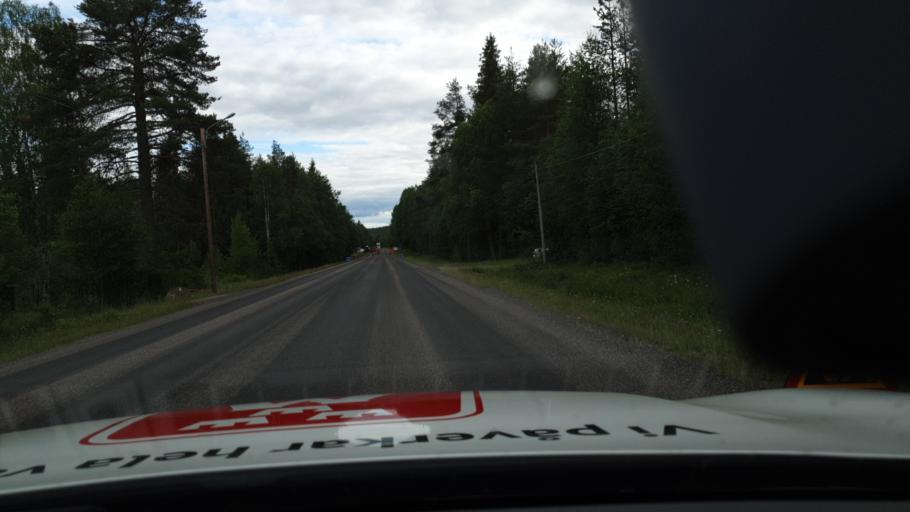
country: SE
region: Norrbotten
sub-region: Overkalix Kommun
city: OEverkalix
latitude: 66.3192
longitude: 22.8140
